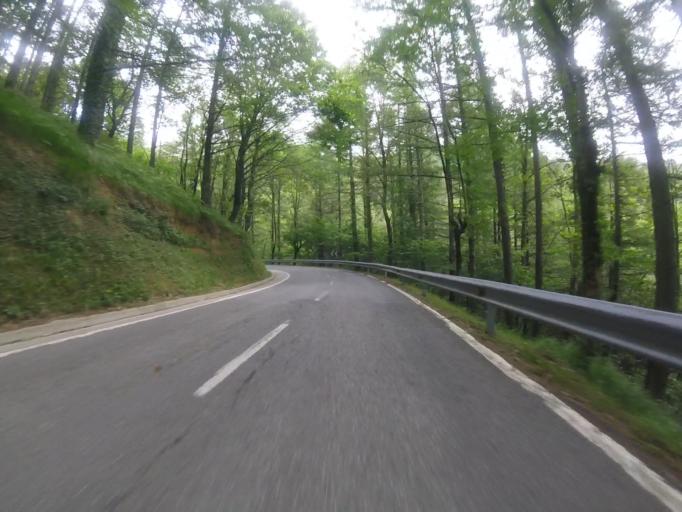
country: ES
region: Navarre
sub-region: Provincia de Navarra
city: Ezkurra
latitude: 43.0858
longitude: -1.8454
